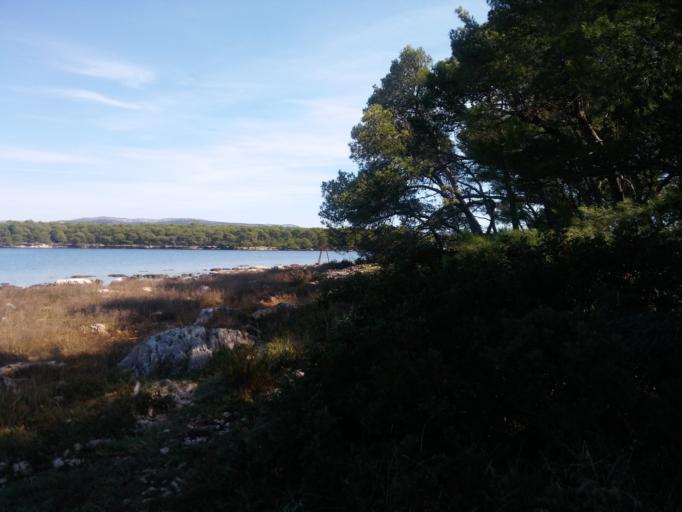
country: HR
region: Sibensko-Kniniska
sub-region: Grad Sibenik
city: Sibenik
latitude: 43.7203
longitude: 15.8550
